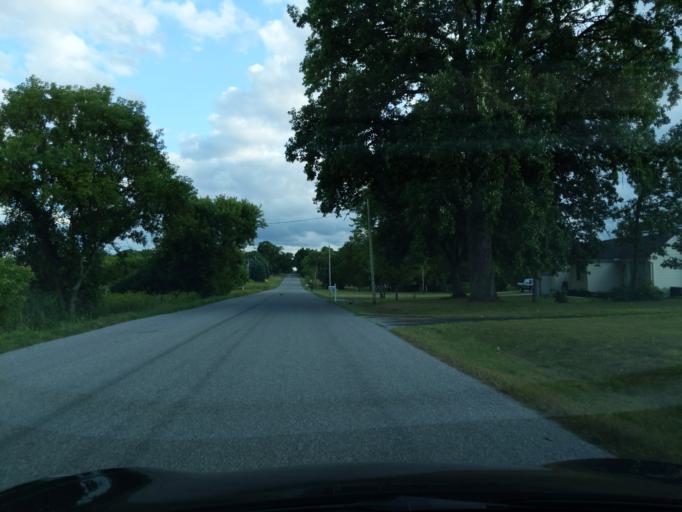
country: US
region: Michigan
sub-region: Ingham County
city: Holt
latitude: 42.6156
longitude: -84.5824
